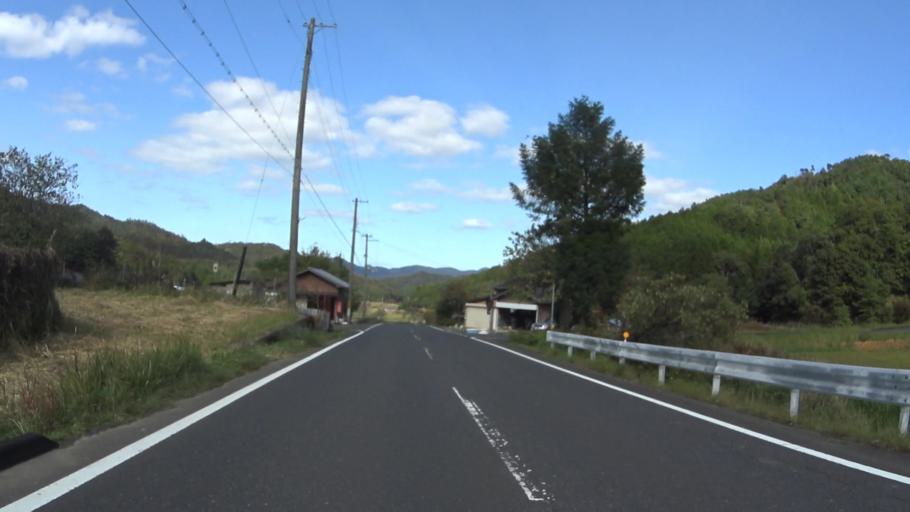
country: JP
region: Hyogo
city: Toyooka
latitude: 35.5462
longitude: 134.9782
